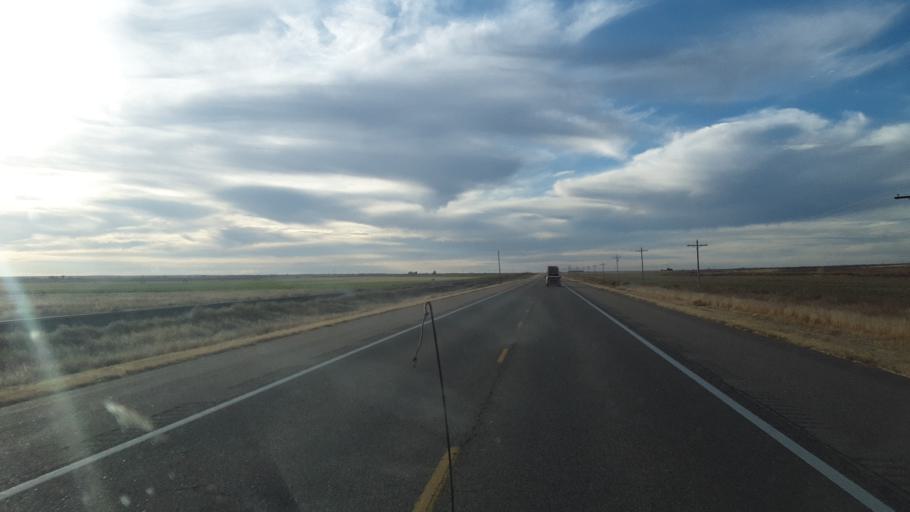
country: US
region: Kansas
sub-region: Hamilton County
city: Syracuse
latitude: 37.9485
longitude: -101.6034
